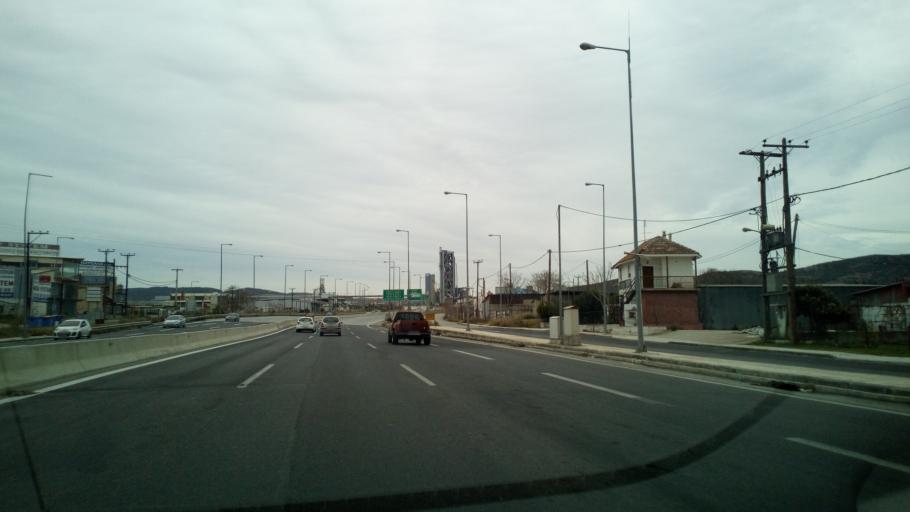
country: GR
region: Central Macedonia
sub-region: Nomos Thessalonikis
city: Efkarpia
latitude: 40.6892
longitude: 22.9435
